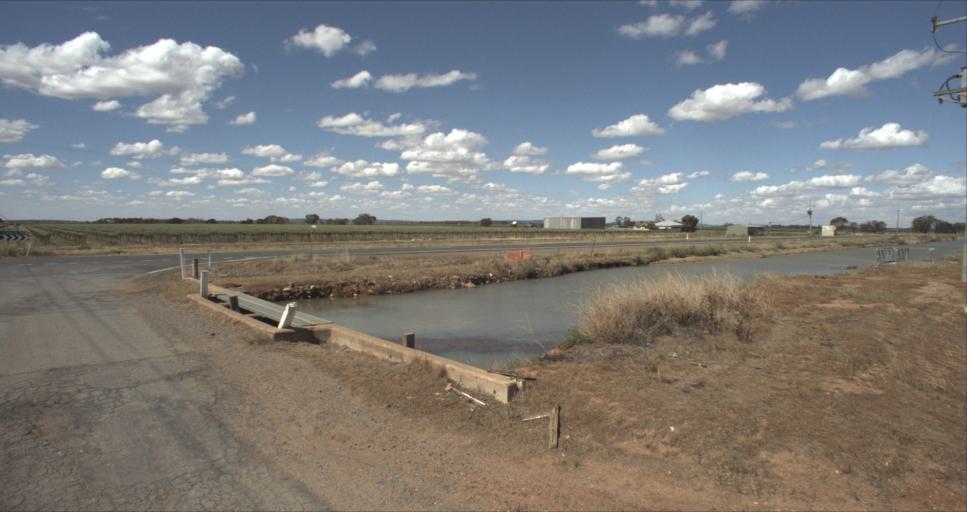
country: AU
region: New South Wales
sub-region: Leeton
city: Leeton
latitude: -34.5087
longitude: 146.2546
